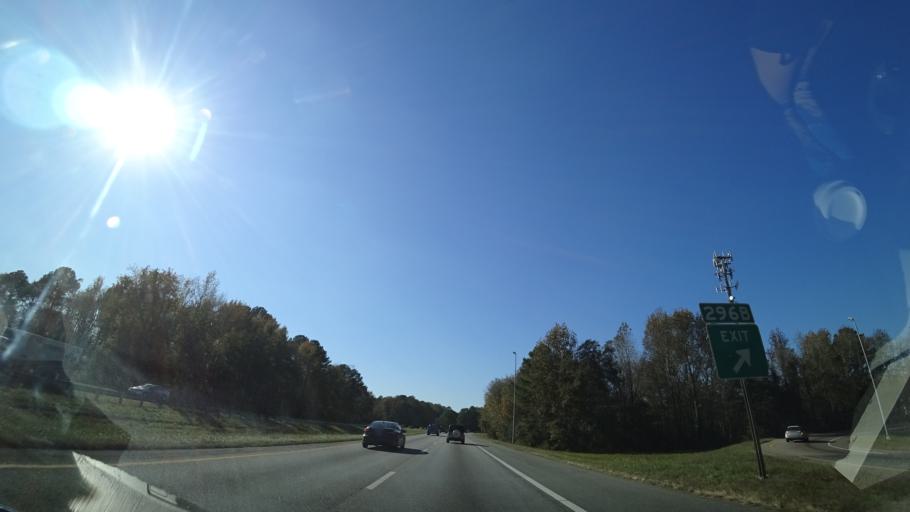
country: US
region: Virginia
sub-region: City of Portsmouth
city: Portsmouth Heights
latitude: 36.7587
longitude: -76.3458
